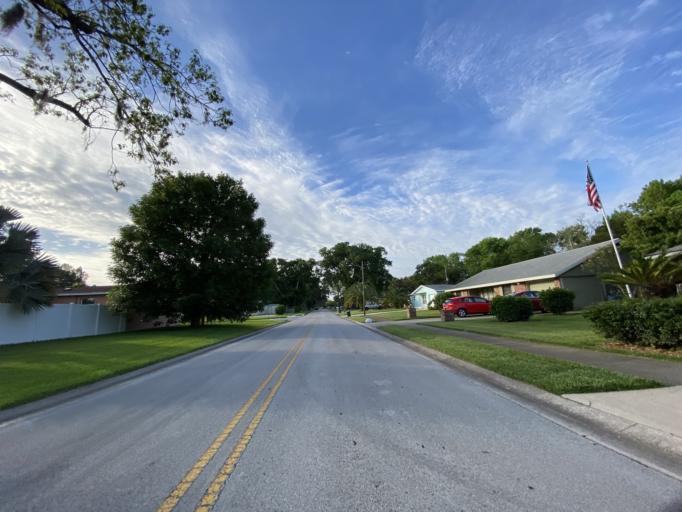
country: US
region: Florida
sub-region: Volusia County
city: South Daytona
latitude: 29.1758
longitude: -81.0153
